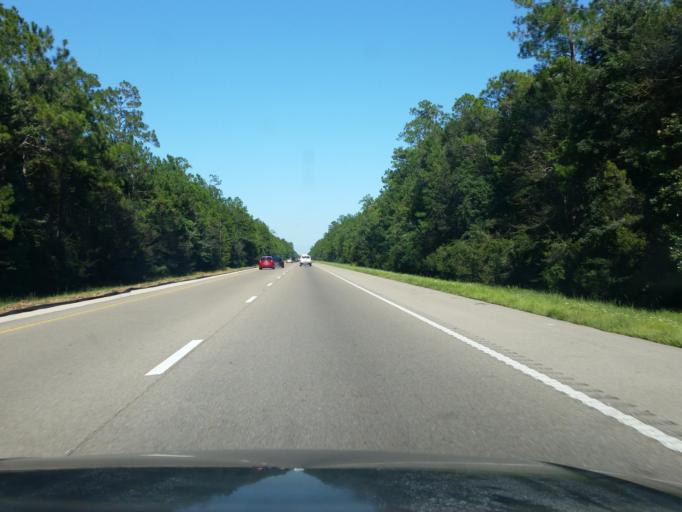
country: US
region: Mississippi
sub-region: Hancock County
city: Pearlington
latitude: 30.3217
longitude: -89.5777
